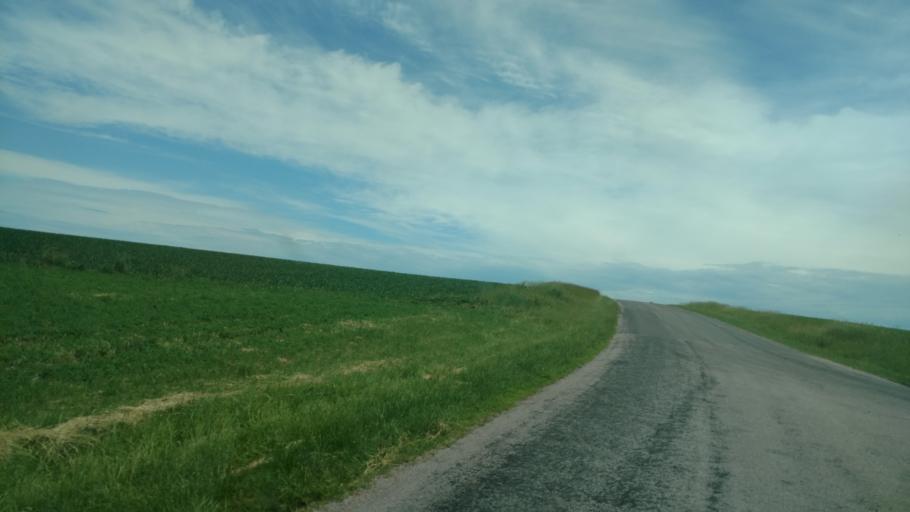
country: US
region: Wisconsin
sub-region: Vernon County
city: Hillsboro
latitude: 43.5757
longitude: -90.3615
